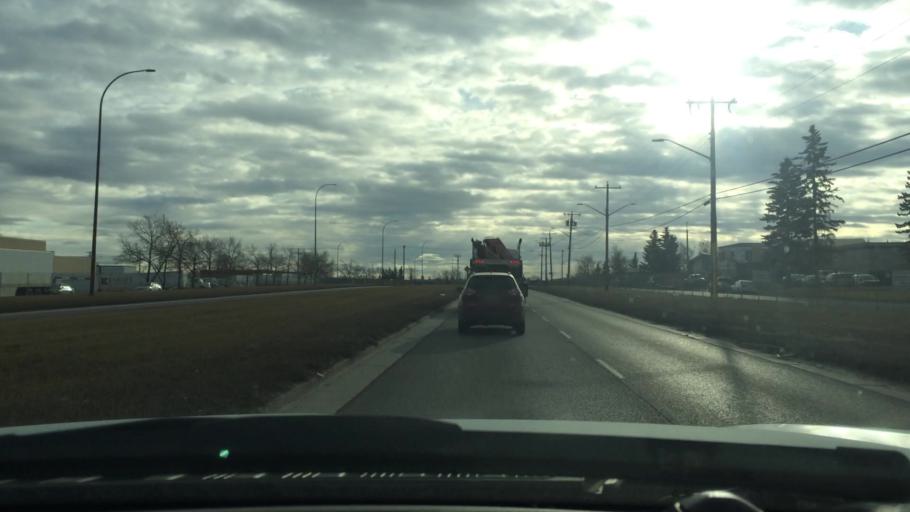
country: CA
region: Alberta
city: Calgary
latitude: 51.0031
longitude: -113.9916
